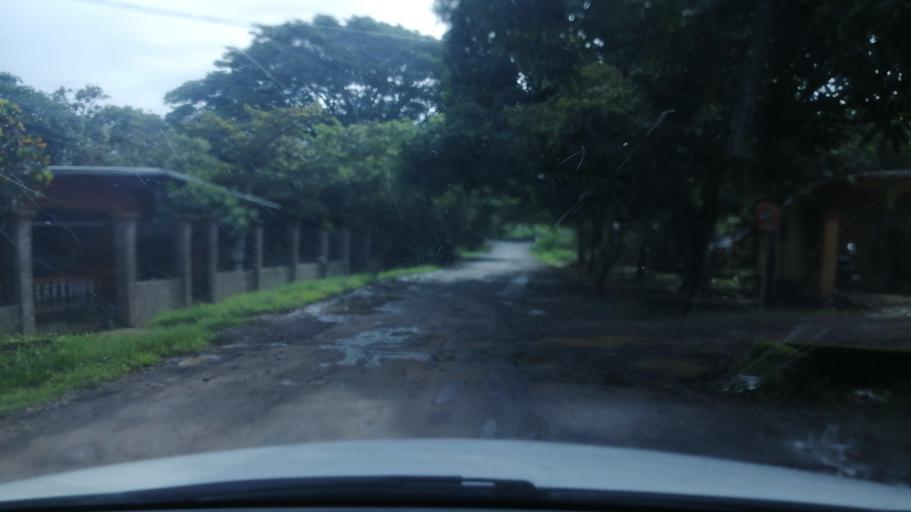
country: PA
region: Chiriqui
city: David
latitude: 8.4068
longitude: -82.4380
